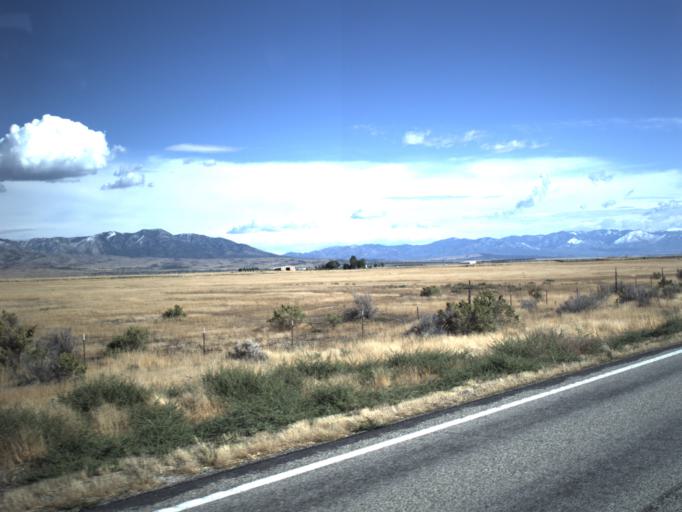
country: US
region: Utah
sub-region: Millard County
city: Delta
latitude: 39.3364
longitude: -112.4900
